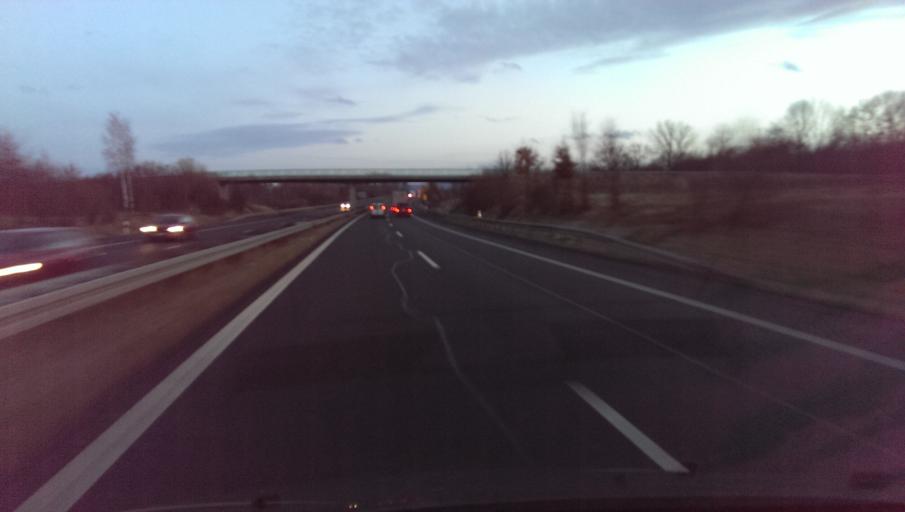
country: DE
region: Saxony-Anhalt
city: Veckenstedt
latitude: 51.8949
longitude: 10.7060
